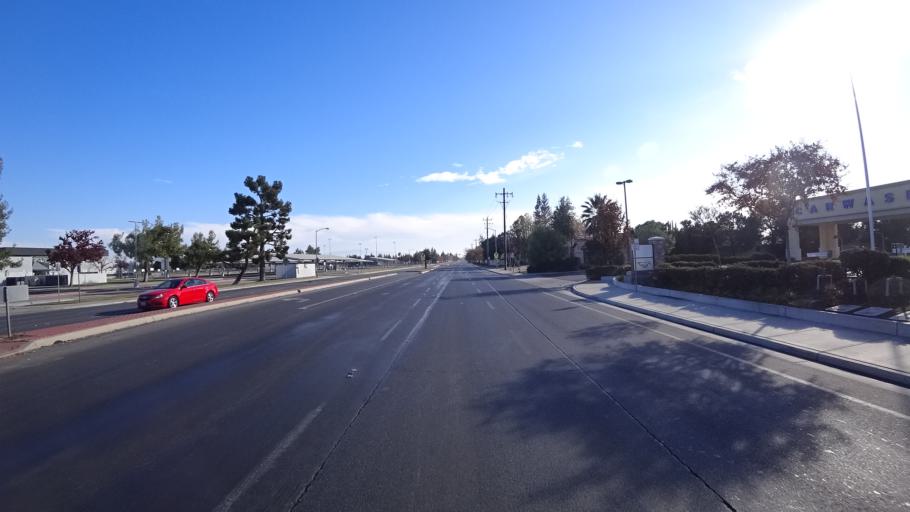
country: US
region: California
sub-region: Kern County
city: Greenacres
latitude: 35.3251
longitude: -119.1266
